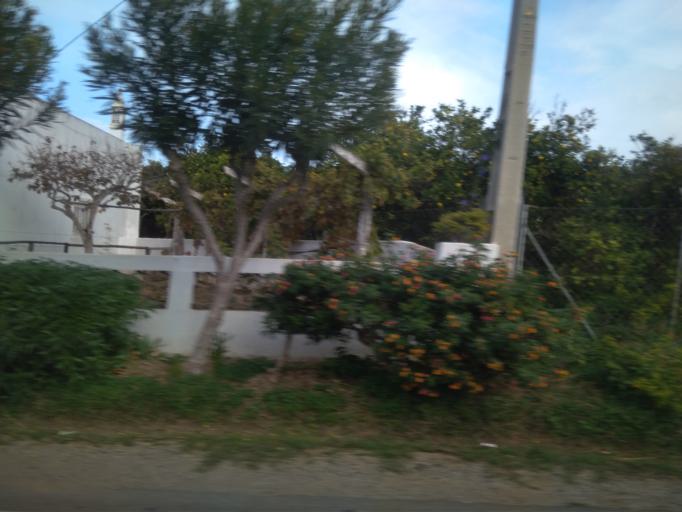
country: PT
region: Faro
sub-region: Faro
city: Santa Barbara de Nexe
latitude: 37.0683
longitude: -7.9565
